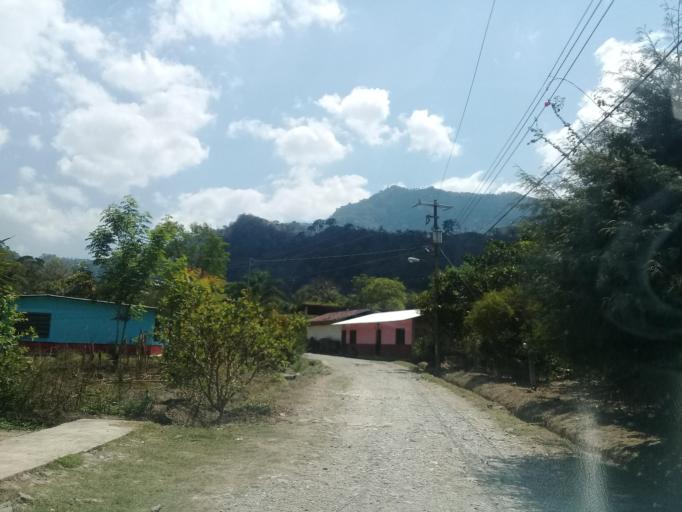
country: MX
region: Veracruz
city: Jalapilla
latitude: 18.8126
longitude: -97.0650
